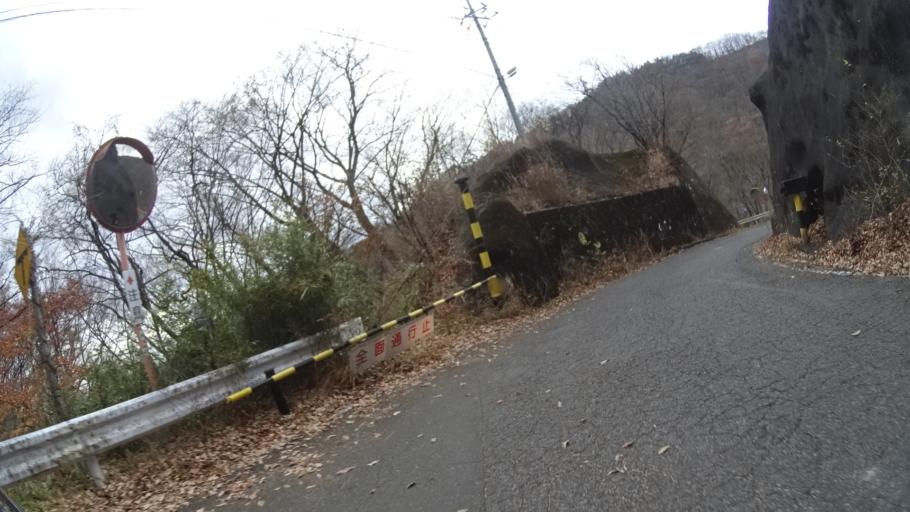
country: JP
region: Gunma
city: Omamacho-omama
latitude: 36.5034
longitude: 139.1812
